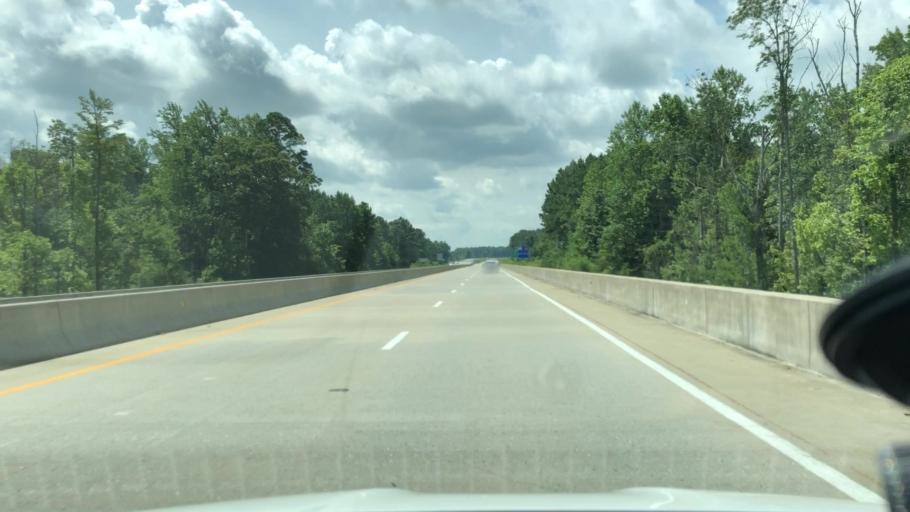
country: US
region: North Carolina
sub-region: Beaufort County
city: Washington
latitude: 35.5207
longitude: -77.0854
